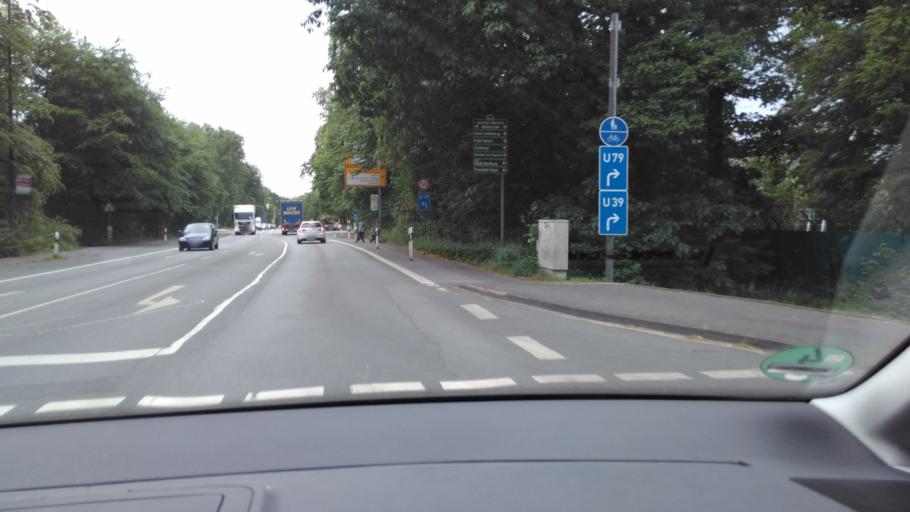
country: DE
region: North Rhine-Westphalia
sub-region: Regierungsbezirk Detmold
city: Guetersloh
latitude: 51.8967
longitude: 8.4061
